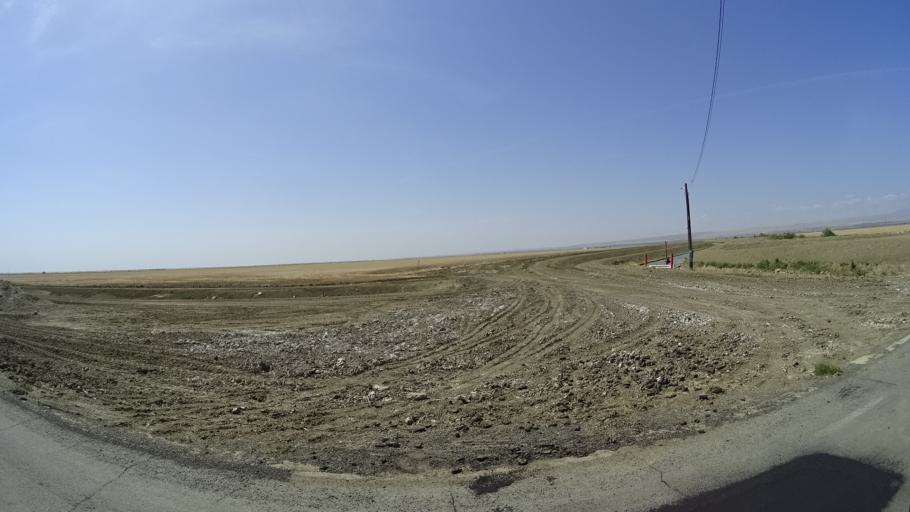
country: US
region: California
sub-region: Kings County
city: Kettleman City
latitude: 36.0941
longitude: -119.9222
